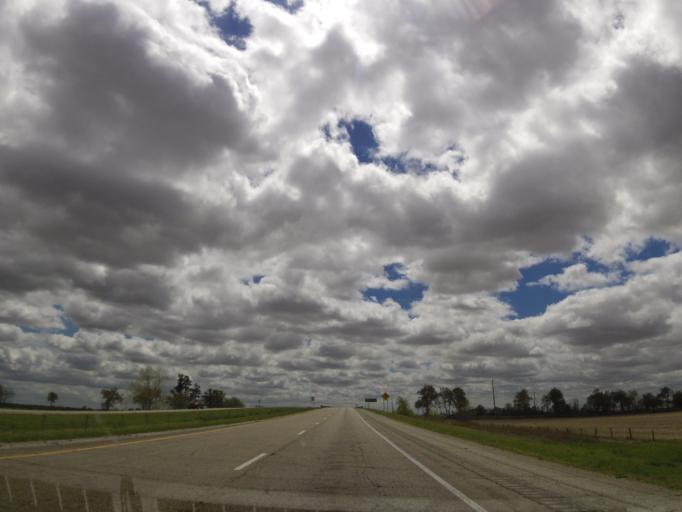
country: US
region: Arkansas
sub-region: Poinsett County
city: Trumann
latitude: 35.6235
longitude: -90.4967
